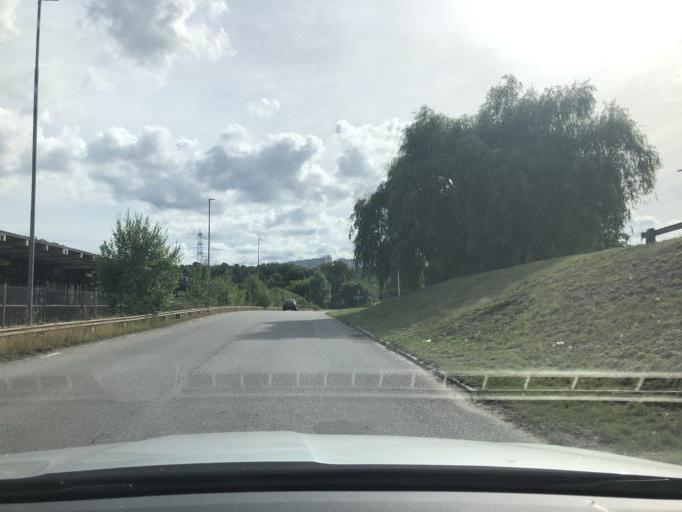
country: SE
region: Stockholm
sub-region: Botkyrka Kommun
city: Fittja
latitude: 59.2476
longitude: 17.8605
